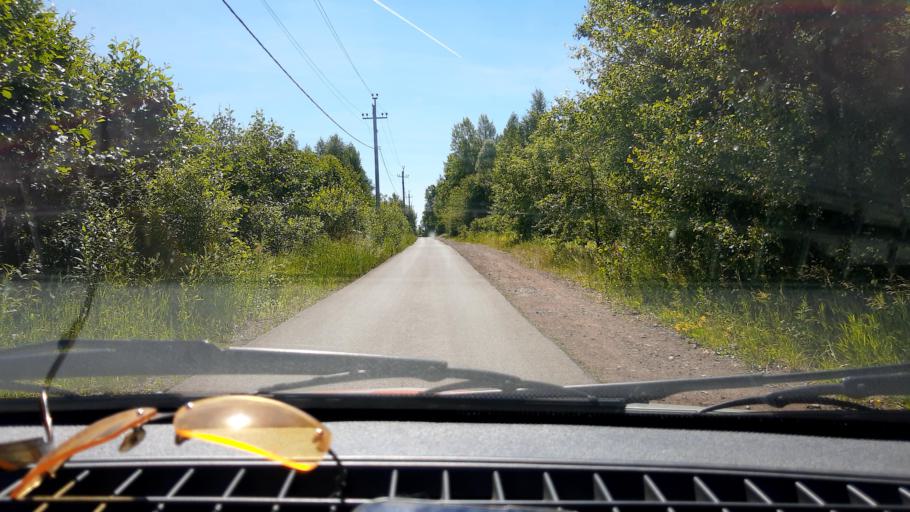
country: RU
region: Bashkortostan
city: Blagoveshchensk
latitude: 54.9705
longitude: 55.8172
